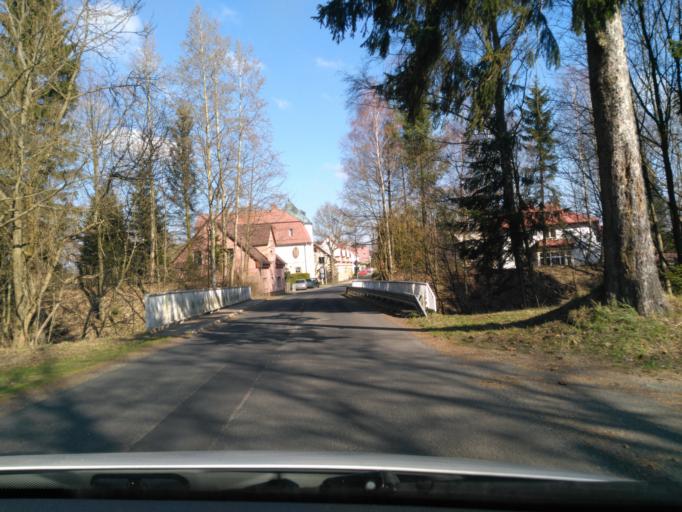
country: CZ
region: Ustecky
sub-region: Okres Chomutov
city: Vejprty
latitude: 50.4822
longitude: 13.0319
